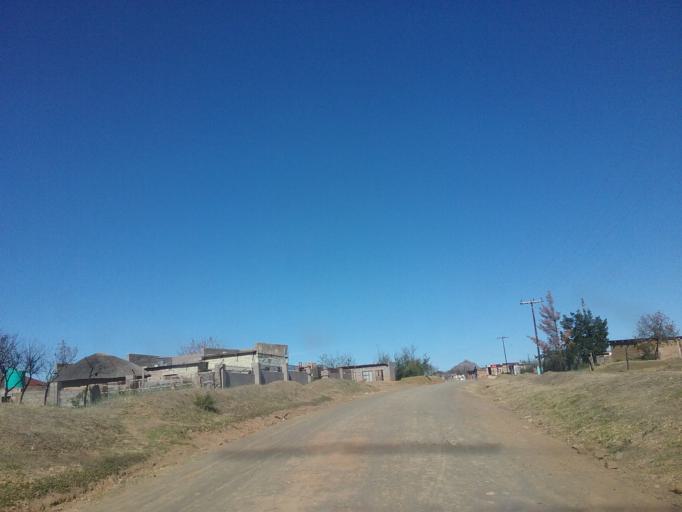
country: LS
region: Maseru
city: Maseru
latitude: -29.4510
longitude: 27.5780
